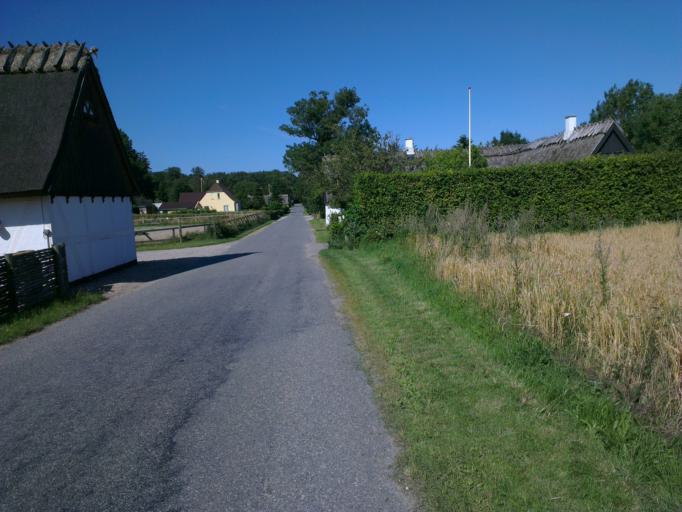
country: DK
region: Capital Region
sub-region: Frederikssund Kommune
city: Skibby
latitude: 55.7133
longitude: 11.9496
